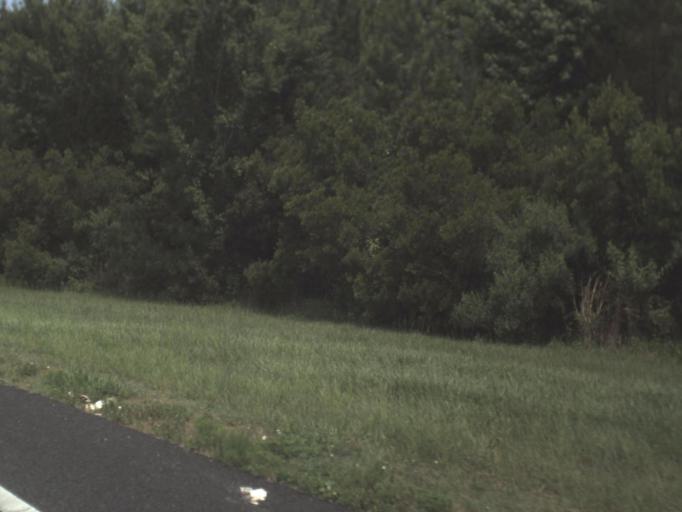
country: US
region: Florida
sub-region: Alachua County
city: Gainesville
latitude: 29.6064
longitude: -82.2233
